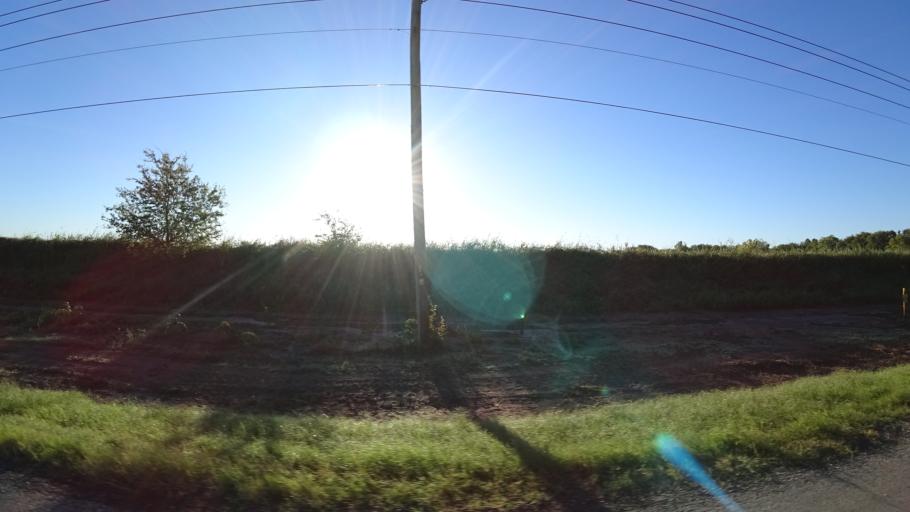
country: US
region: Texas
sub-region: Travis County
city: Hornsby Bend
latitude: 30.2283
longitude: -97.6300
